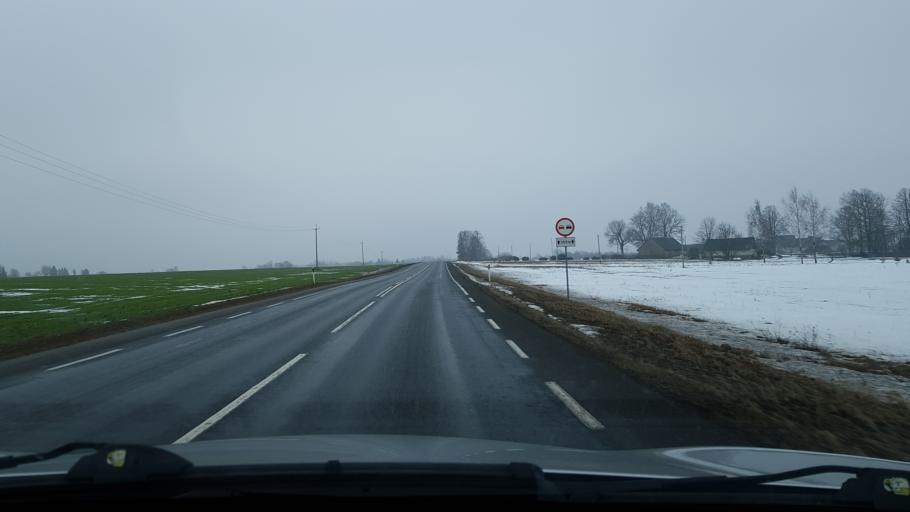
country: EE
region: Viljandimaa
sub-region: Viiratsi vald
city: Viiratsi
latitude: 58.2494
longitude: 25.8434
